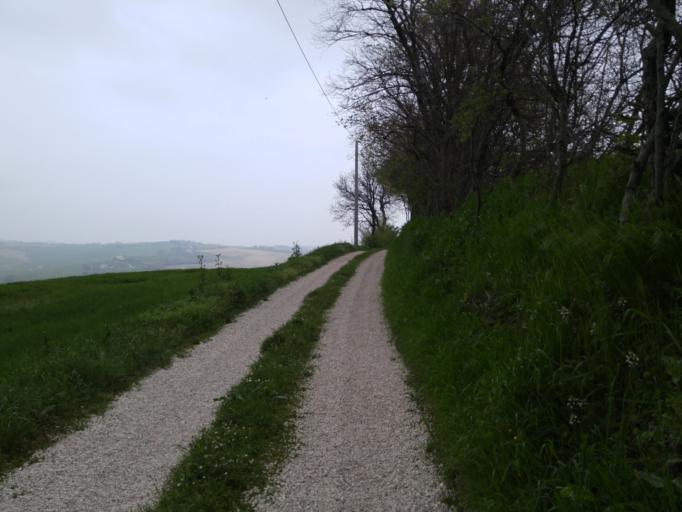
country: IT
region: The Marches
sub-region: Provincia di Pesaro e Urbino
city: Calcinelli
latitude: 43.7705
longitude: 12.9145
